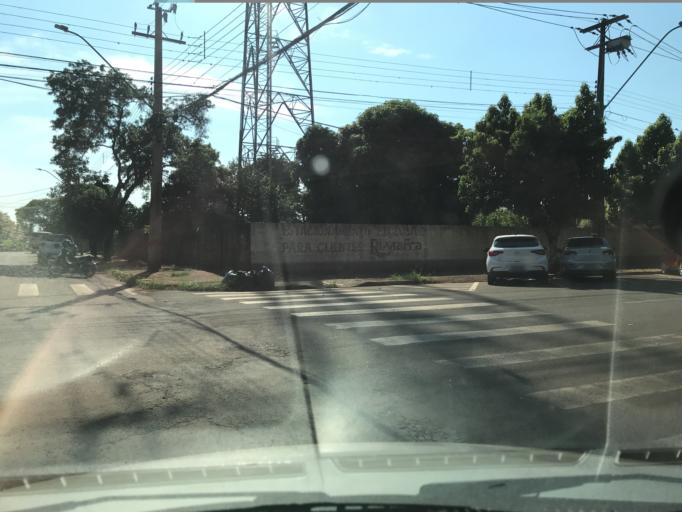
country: BR
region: Parana
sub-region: Palotina
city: Palotina
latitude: -24.2815
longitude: -53.8381
